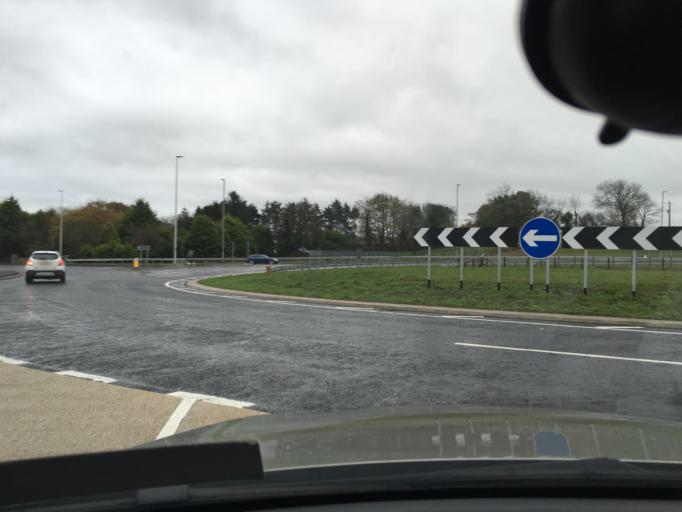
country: GB
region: Northern Ireland
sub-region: Larne District
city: Larne
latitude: 54.8329
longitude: -5.8736
